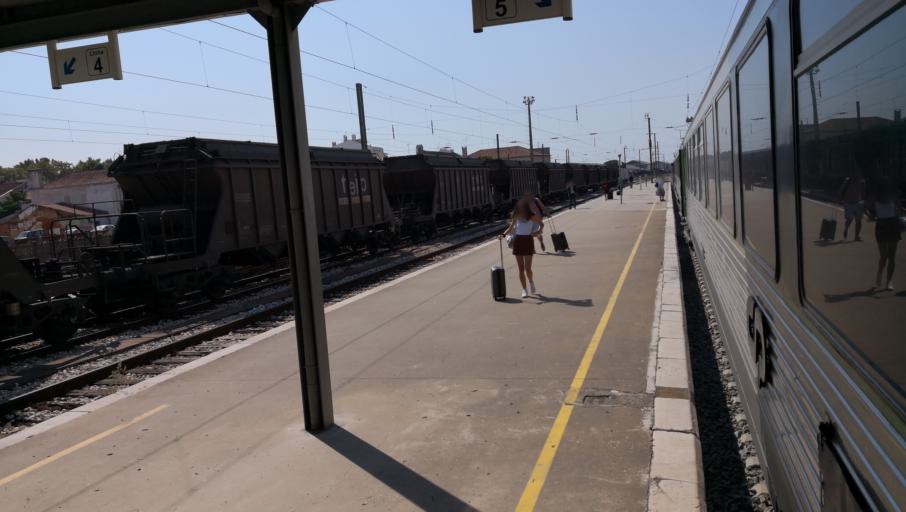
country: PT
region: Santarem
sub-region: Entroncamento
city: Entroncamento
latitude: 39.4614
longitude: -8.4738
